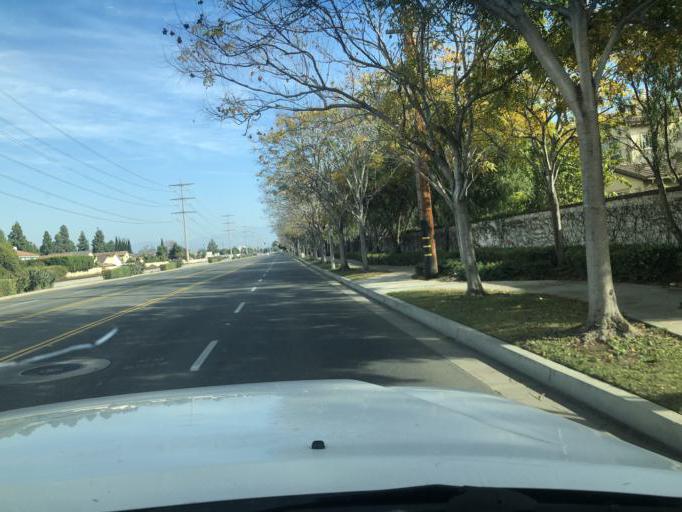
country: US
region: California
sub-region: Orange County
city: Santa Ana
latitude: 33.7036
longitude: -117.8959
